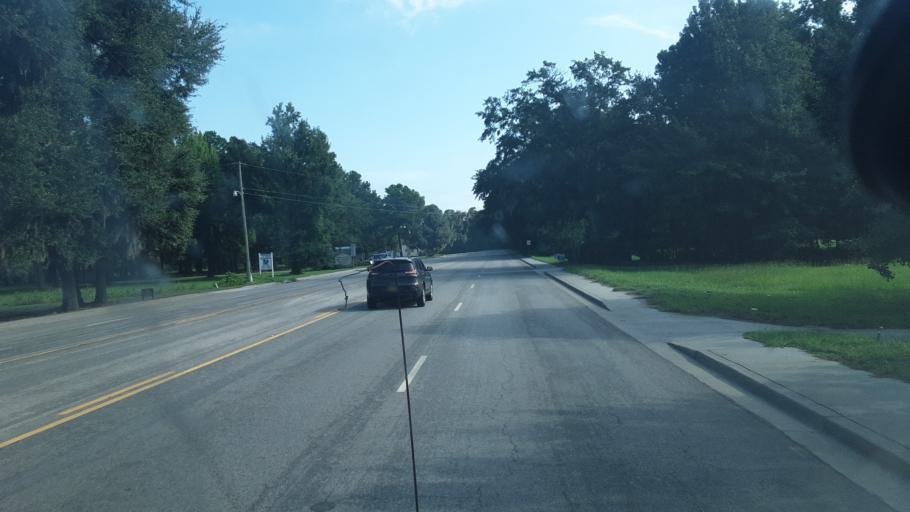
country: US
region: South Carolina
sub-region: Beaufort County
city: Burton
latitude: 32.4108
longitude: -80.7324
